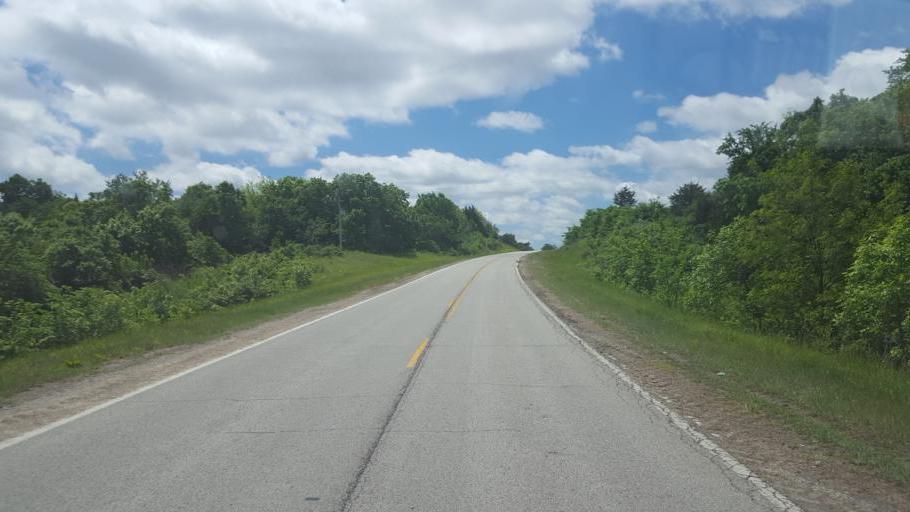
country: US
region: Missouri
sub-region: Harrison County
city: Bethany
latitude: 40.3899
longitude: -94.0019
